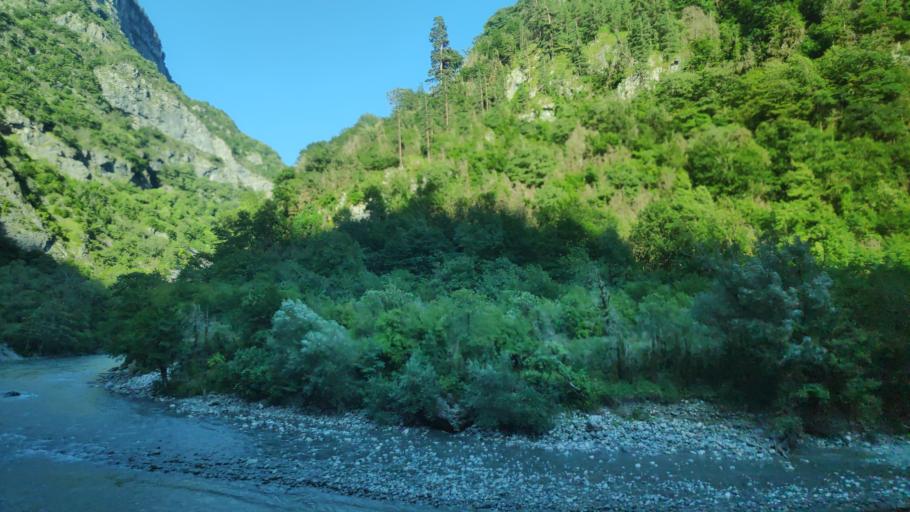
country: GE
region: Abkhazia
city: Gagra
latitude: 43.3676
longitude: 40.4567
